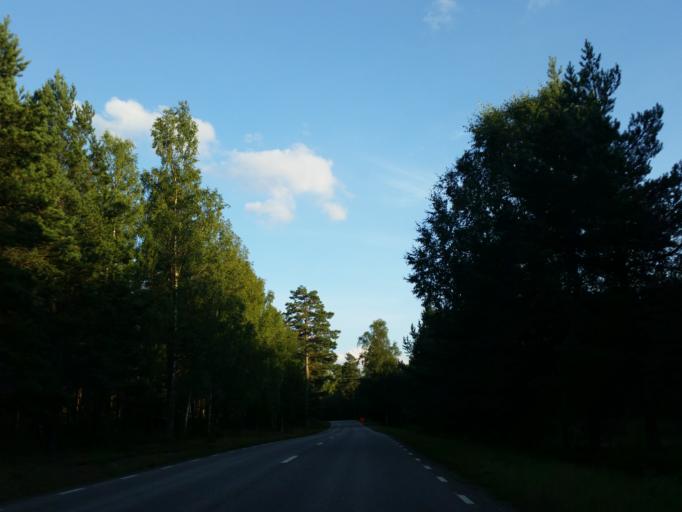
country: SE
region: Stockholm
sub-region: Sodertalje Kommun
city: Soedertaelje
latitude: 59.2415
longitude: 17.5422
